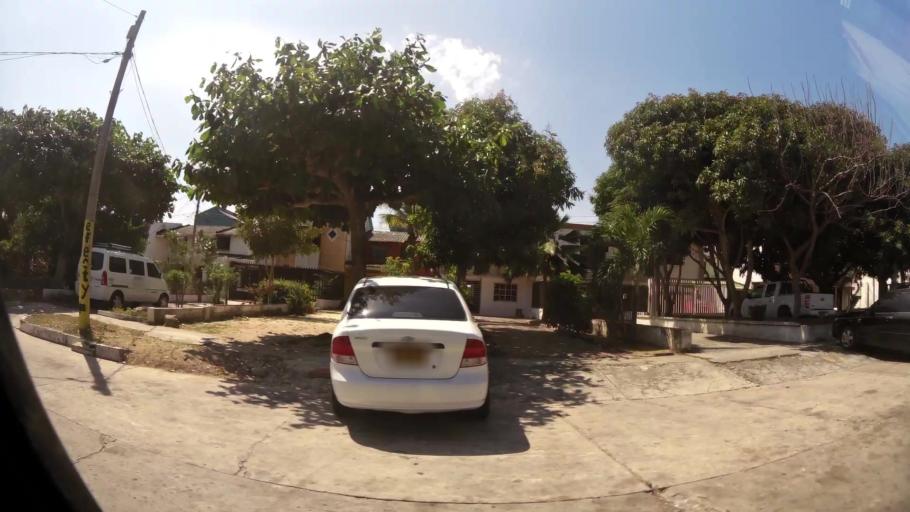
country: CO
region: Atlantico
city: Barranquilla
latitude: 10.9798
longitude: -74.8171
